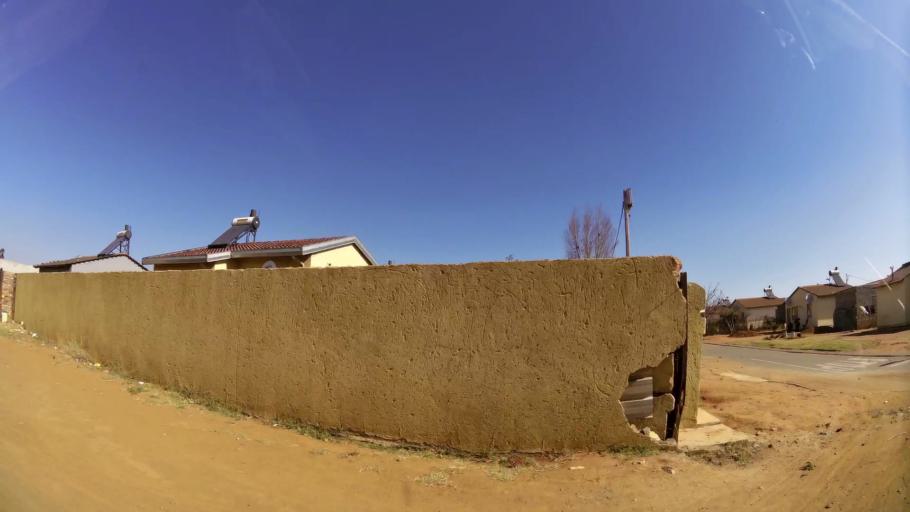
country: ZA
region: Gauteng
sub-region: Ekurhuleni Metropolitan Municipality
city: Tembisa
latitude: -26.0244
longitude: 28.2444
